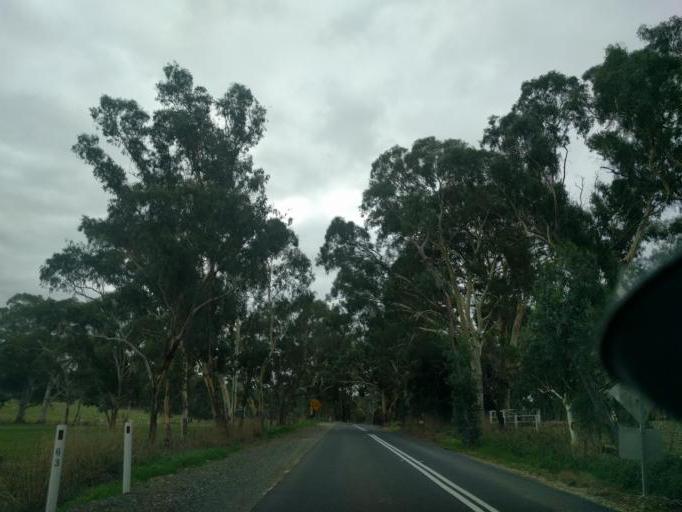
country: AU
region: South Australia
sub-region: Mount Barker
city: Hahndorf
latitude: -35.0751
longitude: 138.7789
